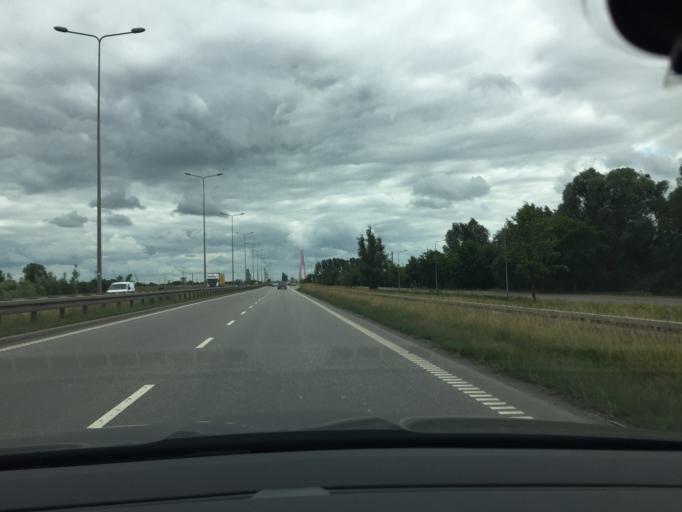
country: PL
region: Pomeranian Voivodeship
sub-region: Gdansk
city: Gdansk
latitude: 54.3698
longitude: 18.6853
